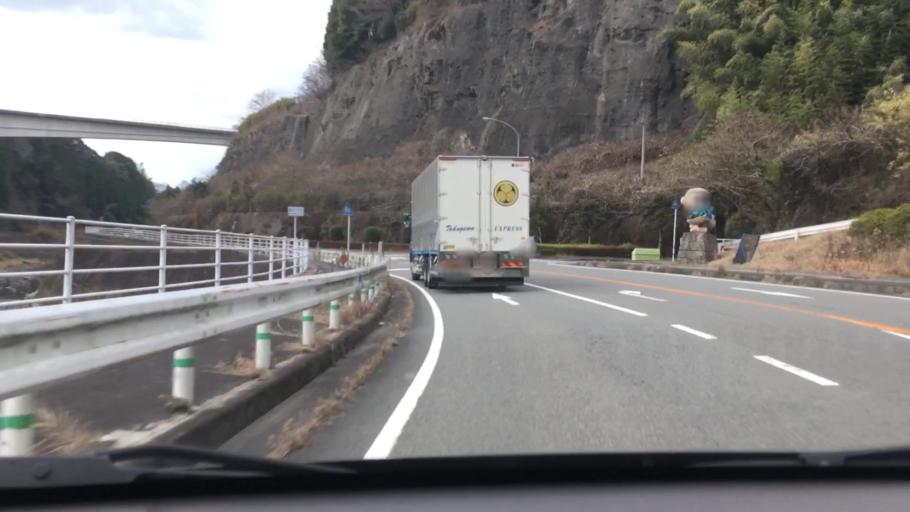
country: JP
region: Oita
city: Usuki
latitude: 33.0689
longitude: 131.6542
